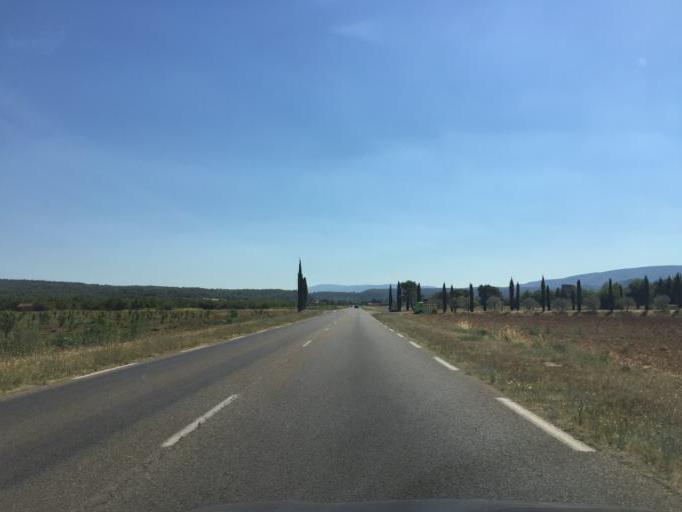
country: FR
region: Provence-Alpes-Cote d'Azur
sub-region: Departement du Vaucluse
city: Oppede
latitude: 43.8626
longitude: 5.1757
